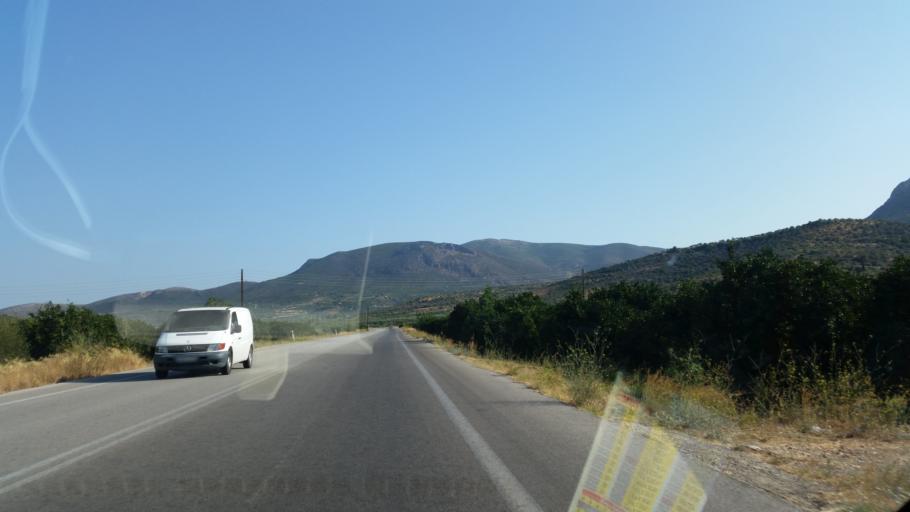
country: GR
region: Peloponnese
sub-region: Nomos Argolidos
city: Koutsopodi
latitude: 37.7300
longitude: 22.7366
